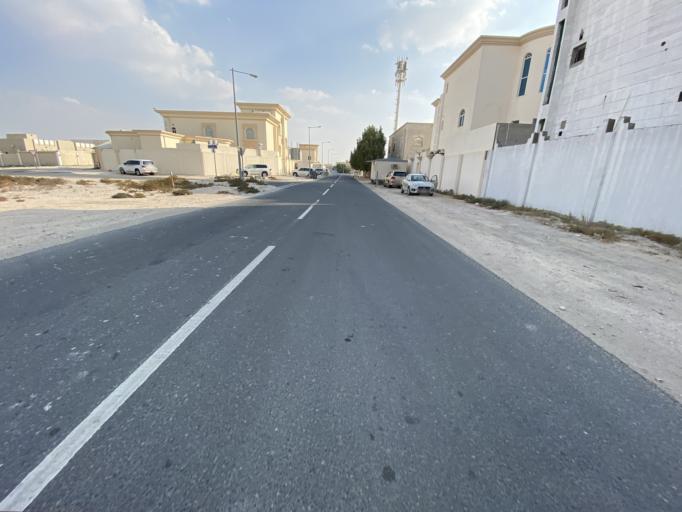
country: QA
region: Baladiyat ar Rayyan
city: Ar Rayyan
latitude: 25.2373
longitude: 51.3783
